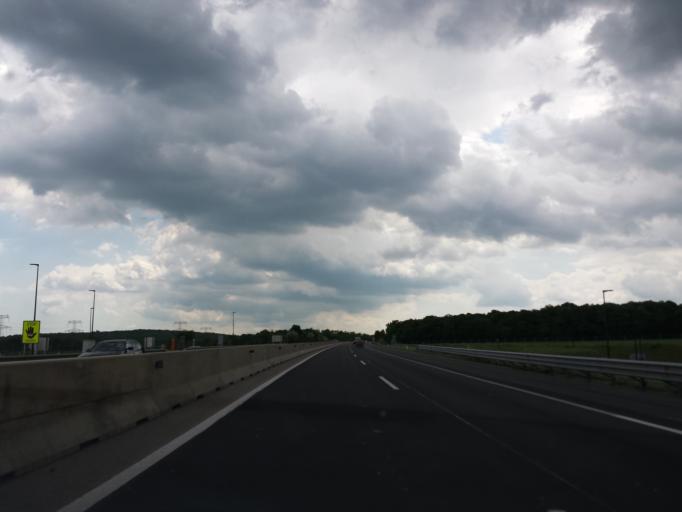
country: AT
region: Lower Austria
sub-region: Politischer Bezirk Wien-Umgebung
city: Fischamend Dorf
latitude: 48.0943
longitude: 16.6612
